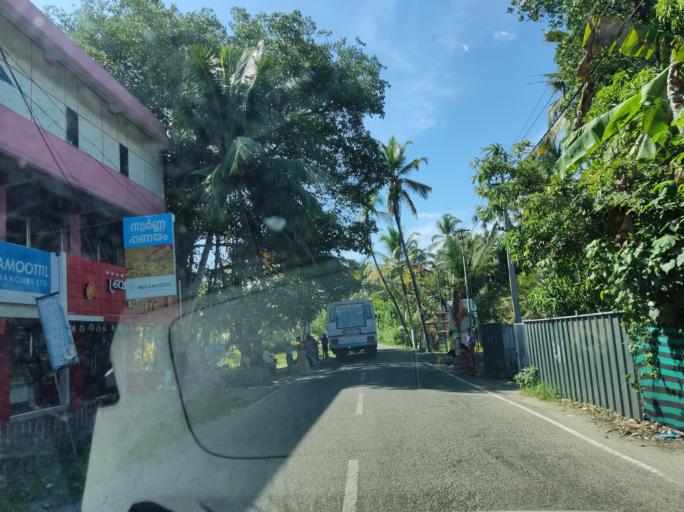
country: IN
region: Kerala
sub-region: Alappuzha
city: Kayankulam
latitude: 9.2329
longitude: 76.4197
